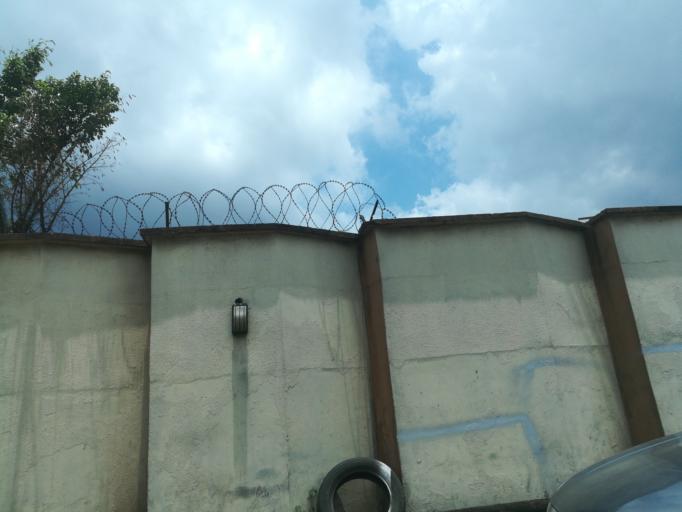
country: NG
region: Lagos
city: Somolu
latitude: 6.5545
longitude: 3.3656
